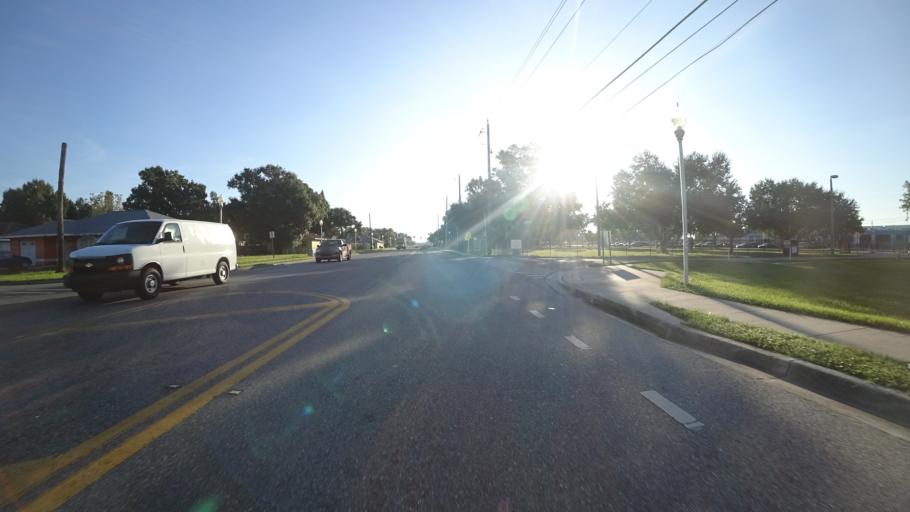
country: US
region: Florida
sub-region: Manatee County
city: Memphis
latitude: 27.5285
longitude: -82.5627
